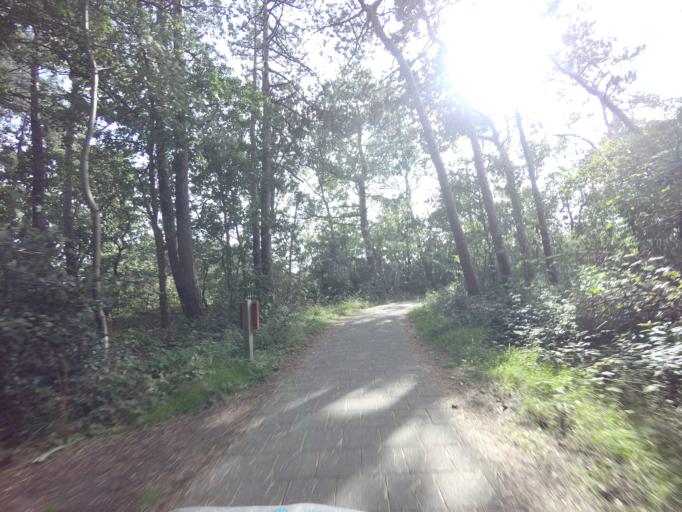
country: NL
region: North Holland
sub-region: Gemeente Texel
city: Den Burg
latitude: 53.0778
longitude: 4.7593
